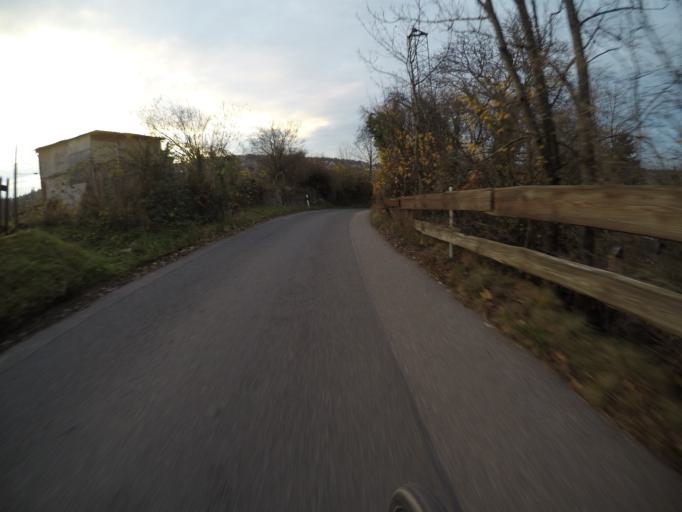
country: DE
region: Baden-Wuerttemberg
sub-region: Regierungsbezirk Stuttgart
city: Ostfildern
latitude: 48.7518
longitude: 9.2509
